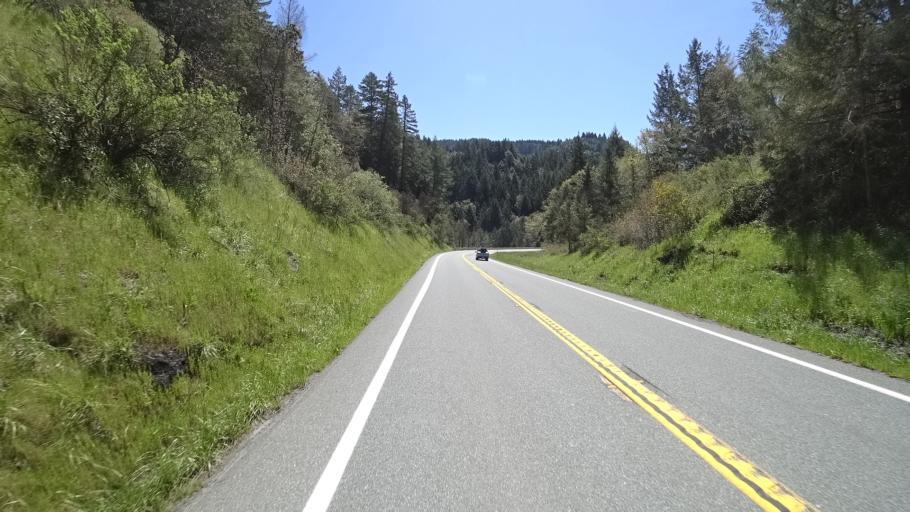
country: US
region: California
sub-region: Humboldt County
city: Willow Creek
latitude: 40.9049
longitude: -123.8055
